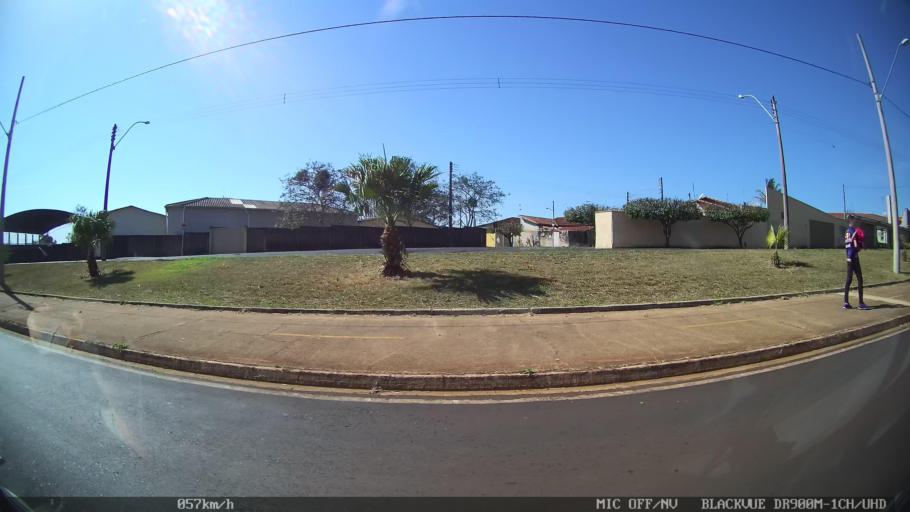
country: BR
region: Sao Paulo
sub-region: Batatais
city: Batatais
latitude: -20.9124
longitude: -47.5830
